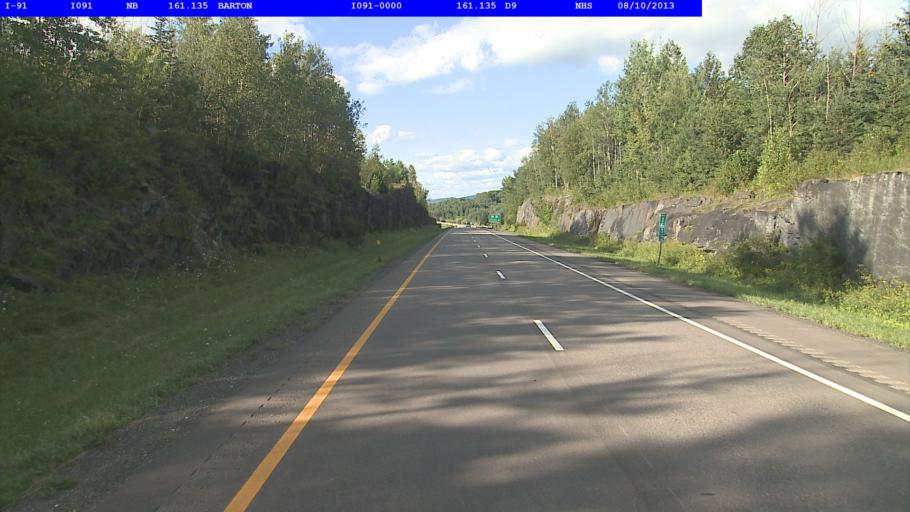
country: US
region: Vermont
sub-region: Orleans County
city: Newport
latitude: 44.8027
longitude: -72.2138
